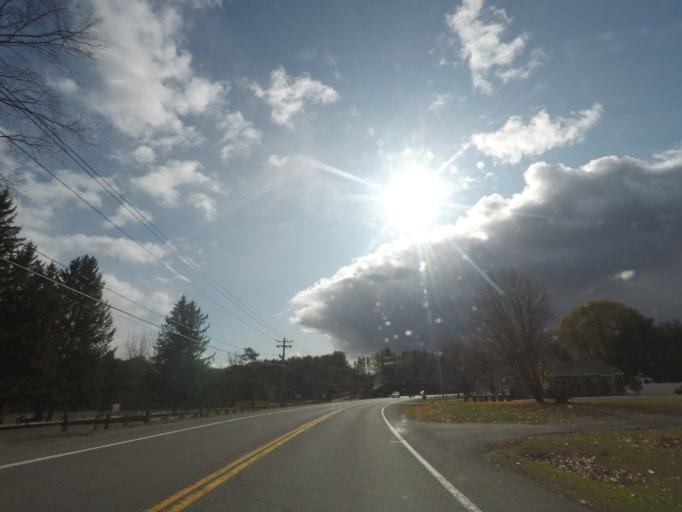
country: US
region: New York
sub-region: Saratoga County
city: Country Knolls
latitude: 42.8993
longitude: -73.8185
